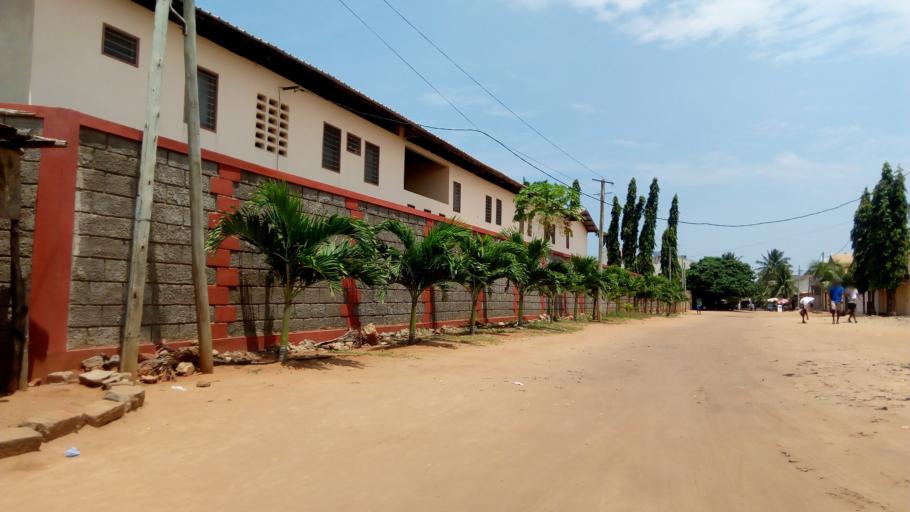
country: TG
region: Maritime
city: Lome
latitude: 6.1837
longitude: 1.1756
